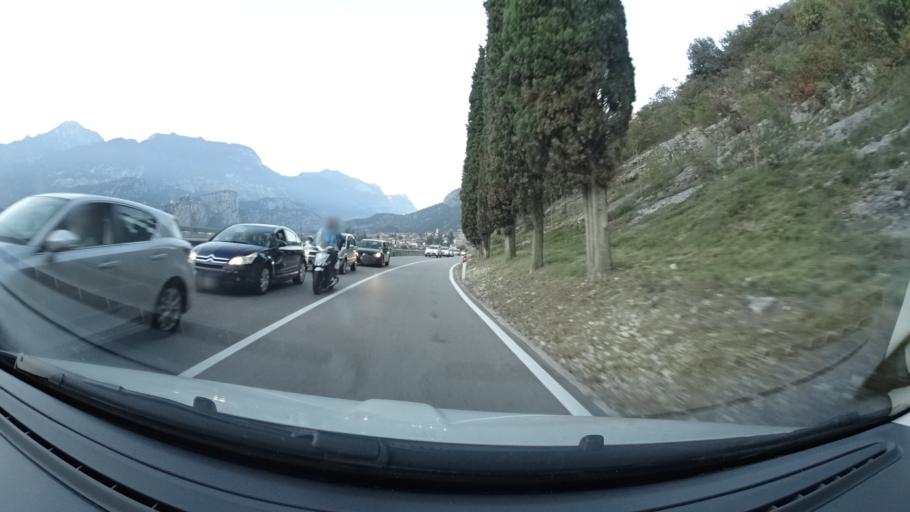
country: IT
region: Trentino-Alto Adige
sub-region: Provincia di Trento
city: Bolognano-Vignole
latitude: 45.9028
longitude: 10.9003
